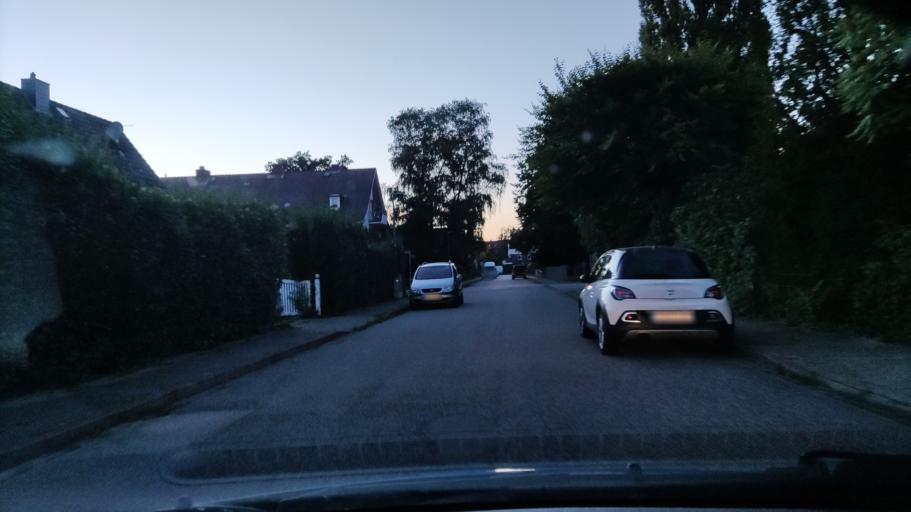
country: DE
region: Schleswig-Holstein
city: Wedel
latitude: 53.5733
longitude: 9.7116
